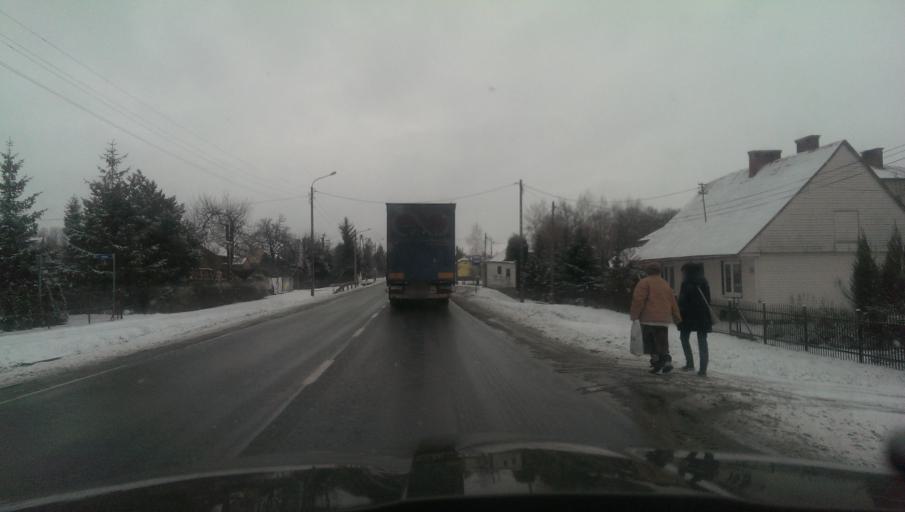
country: PL
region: Subcarpathian Voivodeship
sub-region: Powiat sanocki
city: Nowosielce-Gniewosz
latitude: 49.5684
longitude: 22.0695
